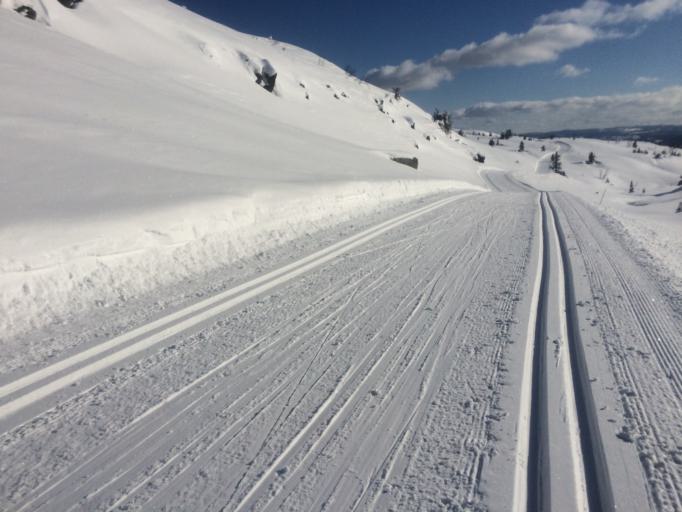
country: NO
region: Oppland
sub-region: Ringebu
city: Ringebu
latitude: 61.3762
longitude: 10.0592
